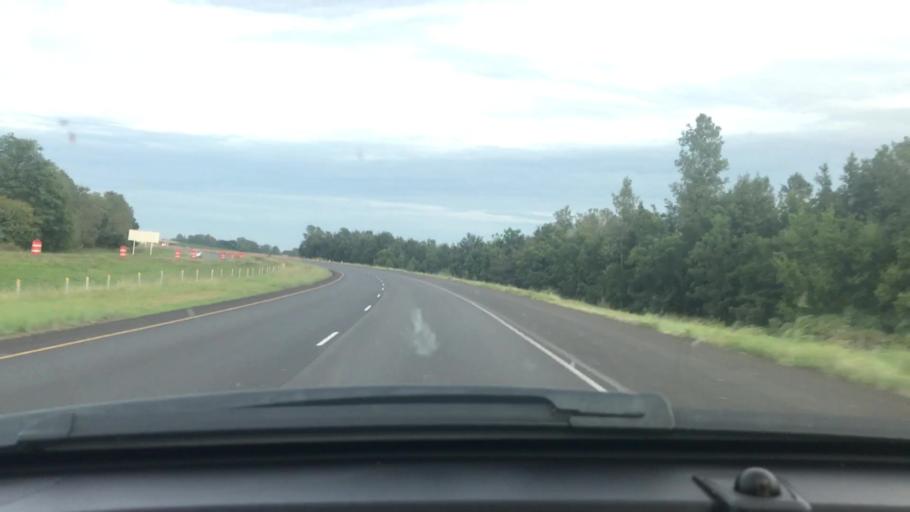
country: US
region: Arkansas
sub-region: Poinsett County
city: Trumann
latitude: 35.6606
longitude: -90.5489
